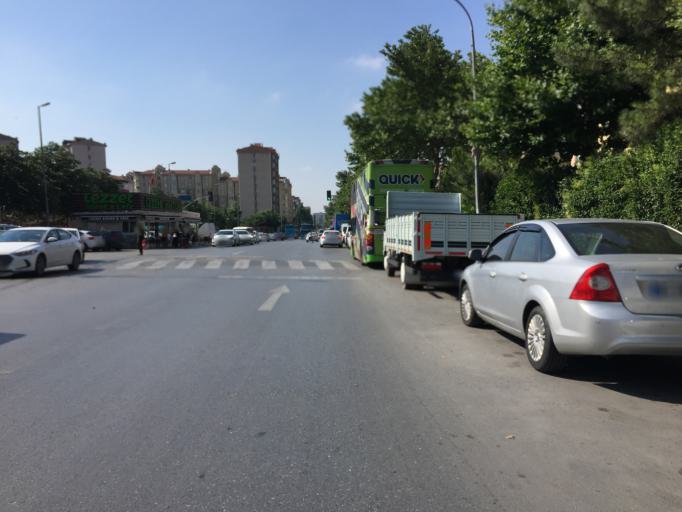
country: TR
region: Istanbul
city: Esenyurt
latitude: 41.0642
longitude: 28.6713
